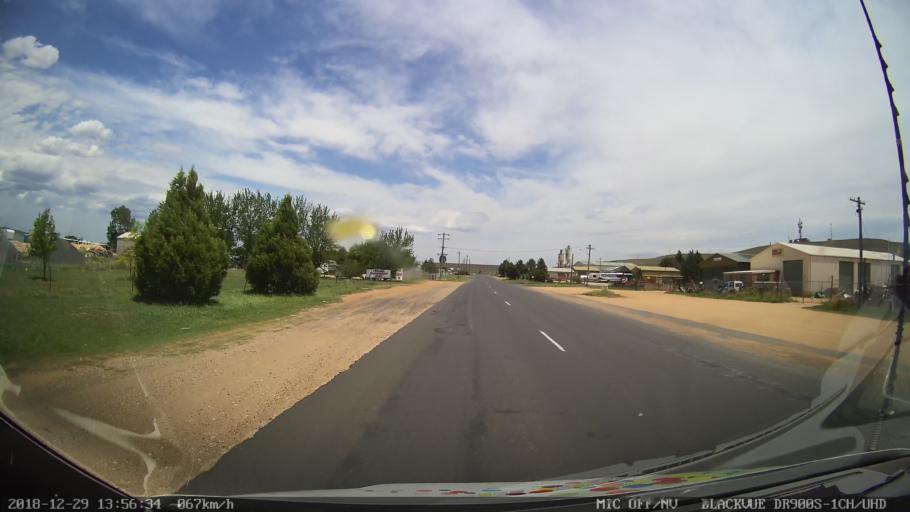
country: AU
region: New South Wales
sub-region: Cooma-Monaro
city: Cooma
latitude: -36.2319
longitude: 149.1459
